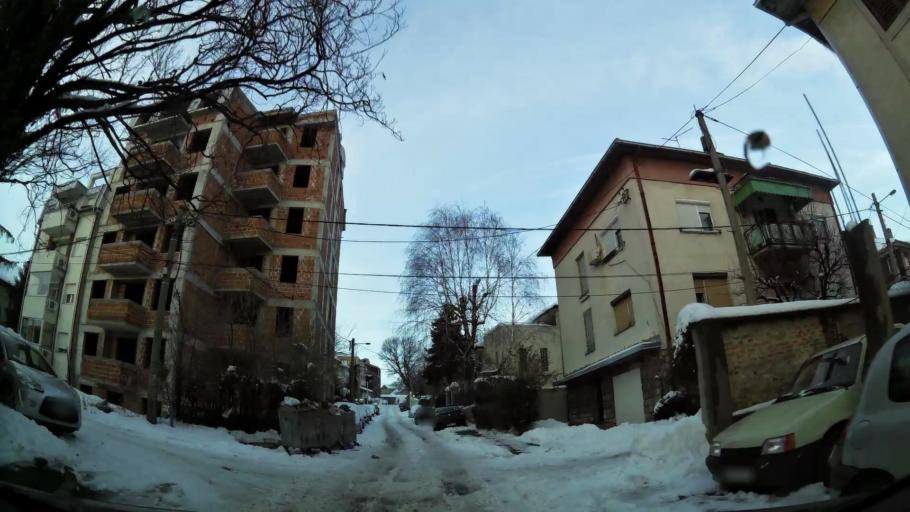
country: RS
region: Central Serbia
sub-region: Belgrade
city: Palilula
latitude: 44.7934
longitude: 20.5156
